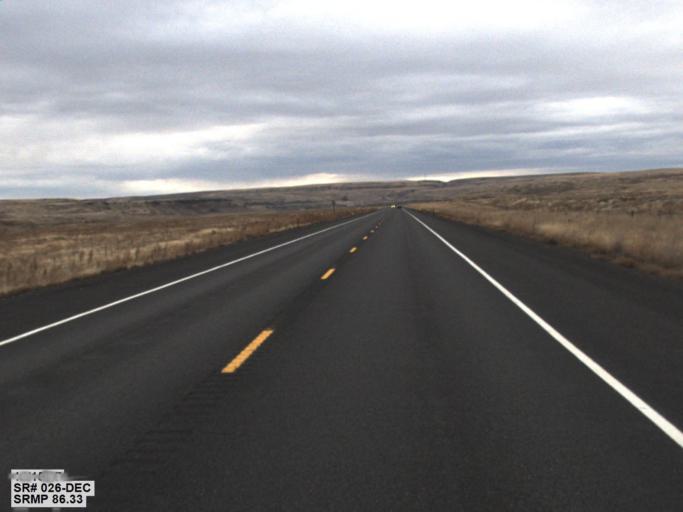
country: US
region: Washington
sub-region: Adams County
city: Ritzville
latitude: 46.7459
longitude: -118.2428
